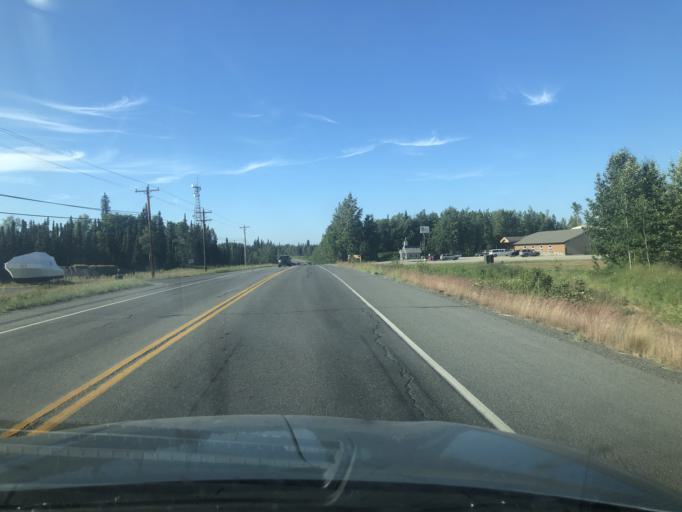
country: US
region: Alaska
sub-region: Kenai Peninsula Borough
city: Ridgeway
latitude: 60.5257
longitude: -151.0810
